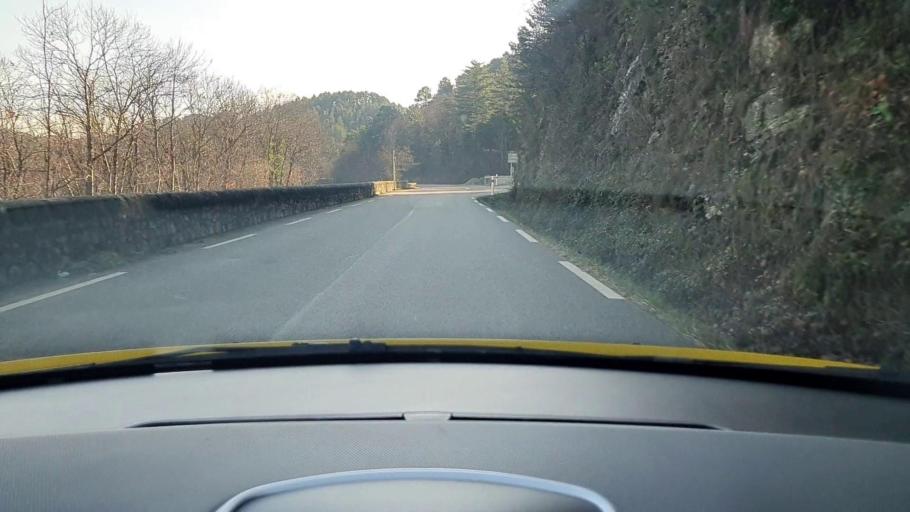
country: FR
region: Languedoc-Roussillon
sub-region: Departement du Gard
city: Branoux-les-Taillades
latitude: 44.3394
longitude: 3.9522
